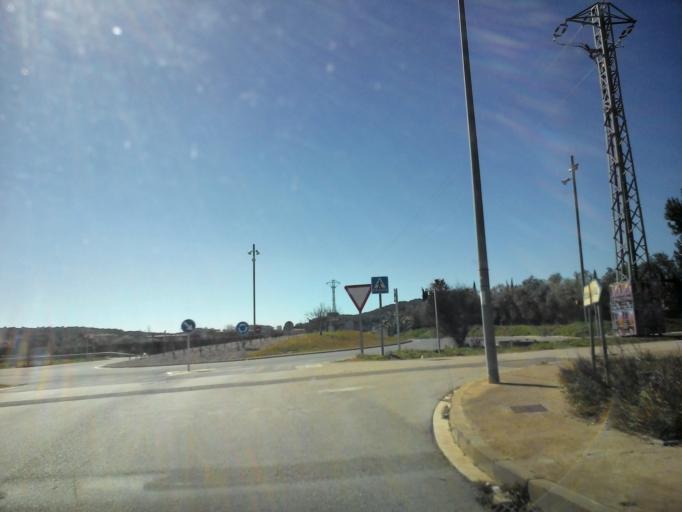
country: ES
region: Catalonia
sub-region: Provincia de Girona
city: Palamos
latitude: 41.8771
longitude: 3.1384
